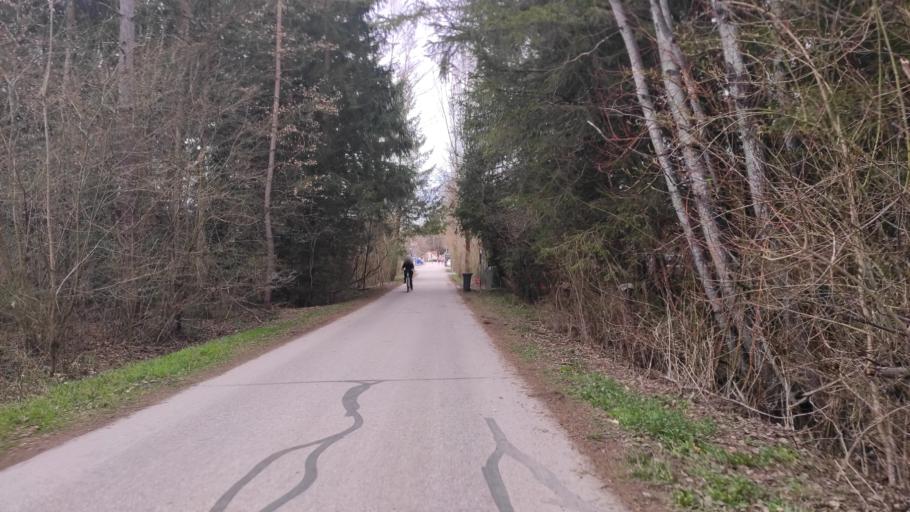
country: DE
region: Bavaria
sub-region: Upper Bavaria
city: Kirchseeon
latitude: 48.0673
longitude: 11.9010
